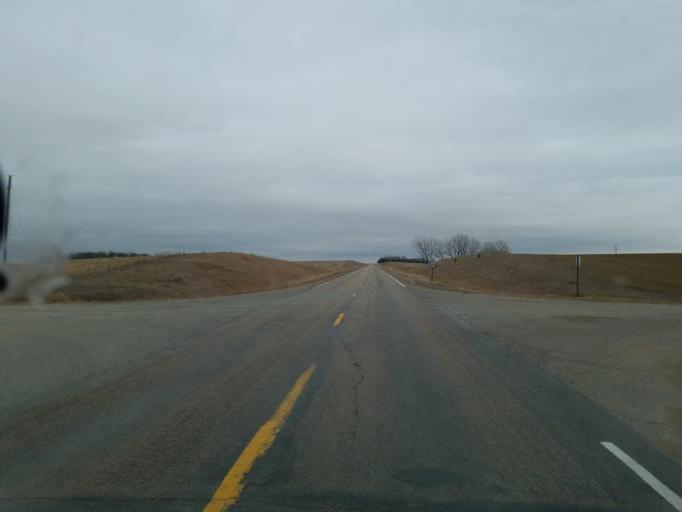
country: US
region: Nebraska
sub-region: Knox County
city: Bloomfield
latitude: 42.5979
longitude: -97.5838
